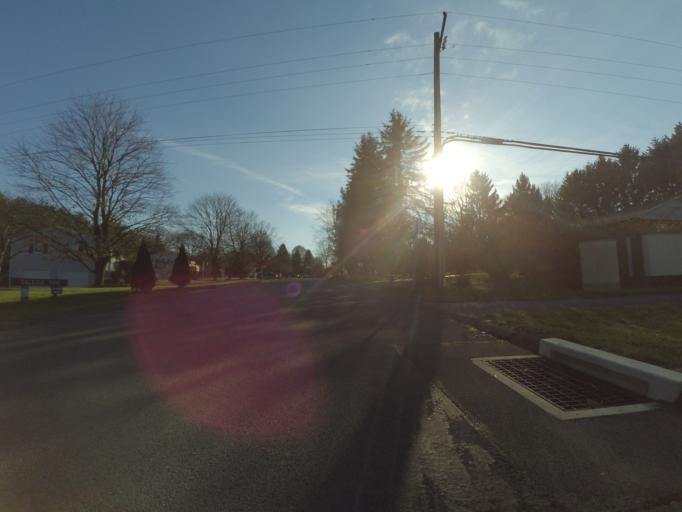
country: US
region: Pennsylvania
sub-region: Centre County
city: Lemont
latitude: 40.7983
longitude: -77.8273
